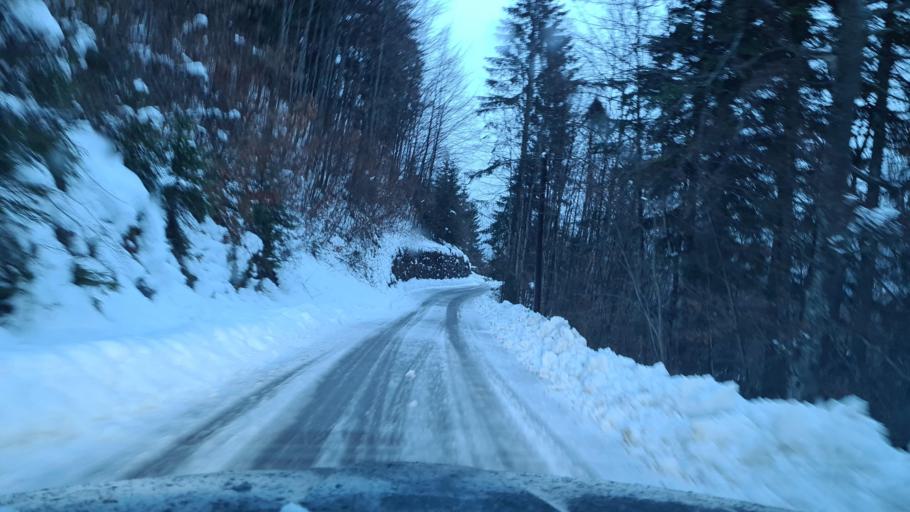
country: AT
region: Salzburg
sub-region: Politischer Bezirk Sankt Johann im Pongau
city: Werfen
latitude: 47.4872
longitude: 13.1571
